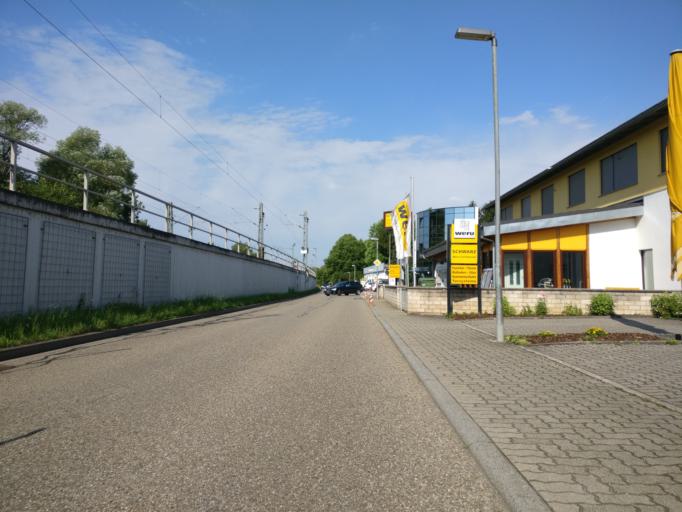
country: DE
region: Baden-Wuerttemberg
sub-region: Karlsruhe Region
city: Weingarten
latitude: 49.0068
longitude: 8.5245
